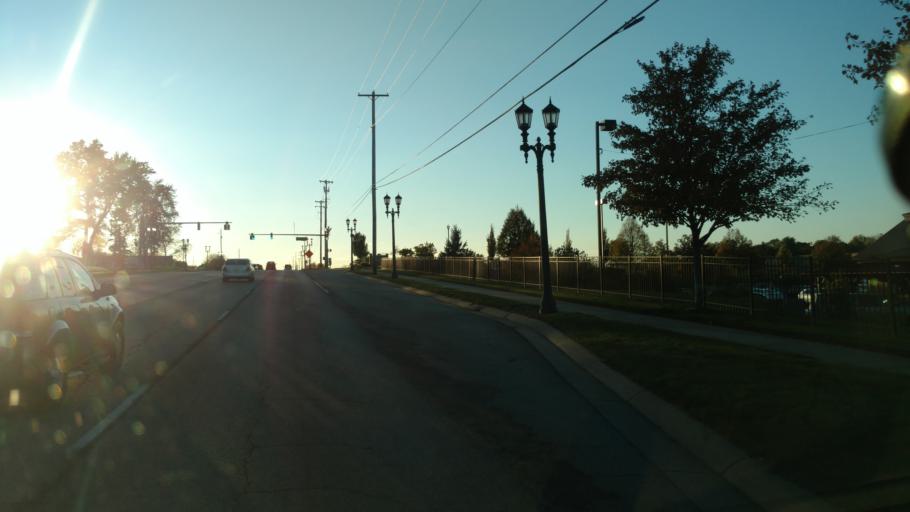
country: US
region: Michigan
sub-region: Ingham County
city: East Lansing
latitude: 42.7608
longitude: -84.5165
